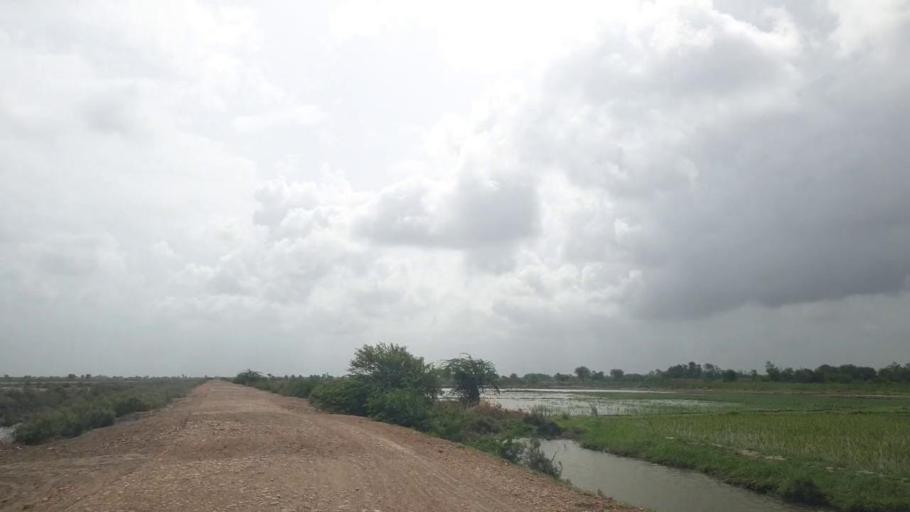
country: PK
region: Sindh
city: Tando Bago
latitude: 24.8273
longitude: 69.0875
